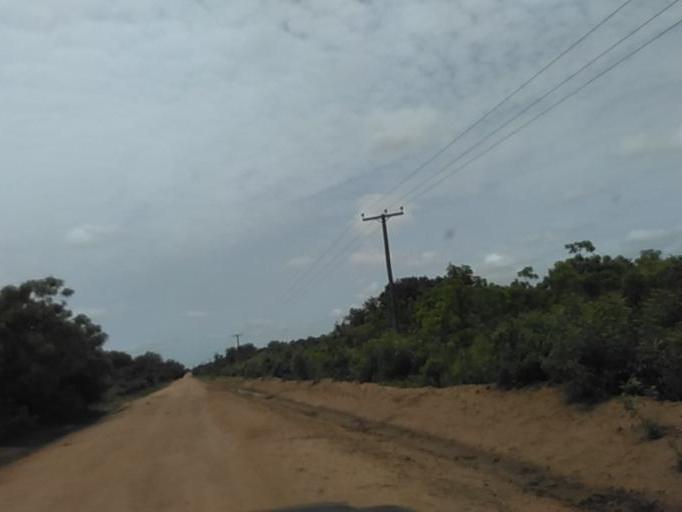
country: GH
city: Akropong
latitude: 6.0554
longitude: 0.2930
